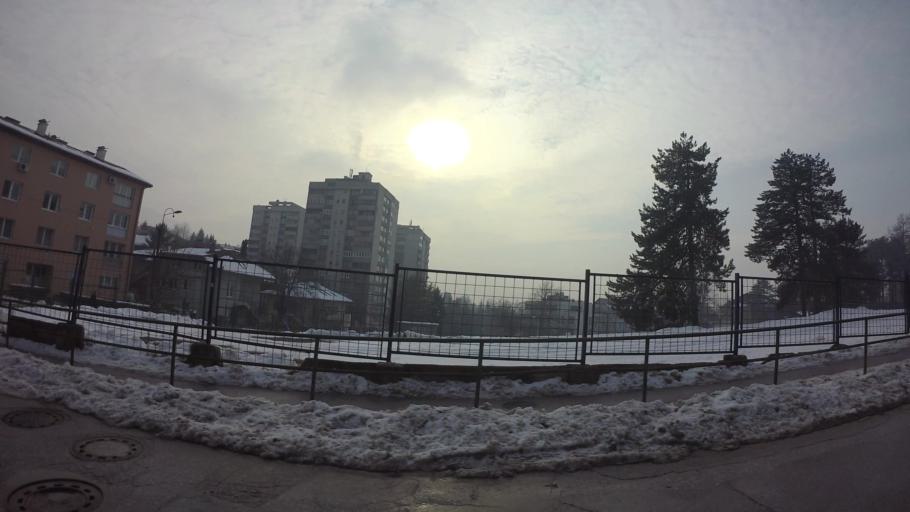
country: BA
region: Federation of Bosnia and Herzegovina
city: Kobilja Glava
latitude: 43.8692
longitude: 18.4188
